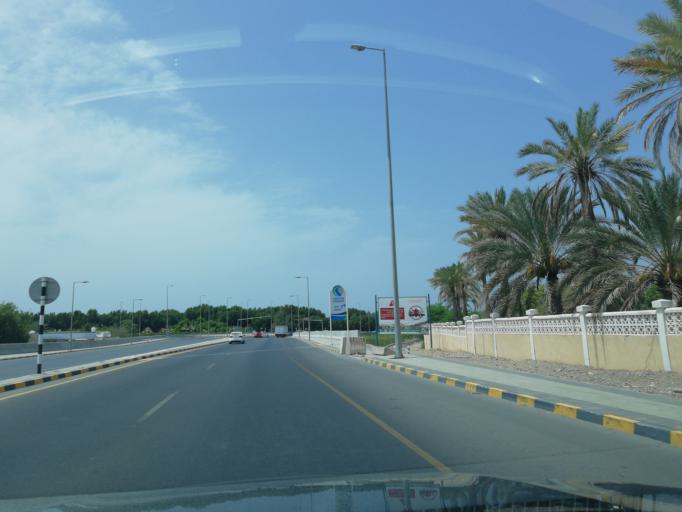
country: OM
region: Muhafazat Masqat
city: As Sib al Jadidah
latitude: 23.6695
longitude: 58.1917
